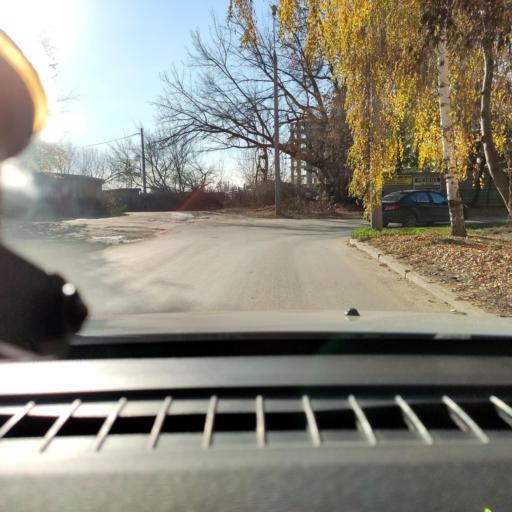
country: RU
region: Samara
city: Samara
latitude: 53.2151
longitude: 50.2650
